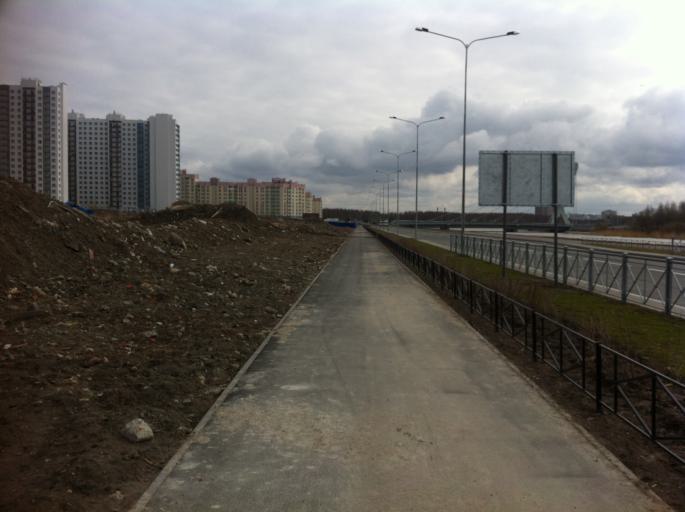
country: RU
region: St.-Petersburg
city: Sosnovaya Polyana
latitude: 59.8631
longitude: 30.1524
